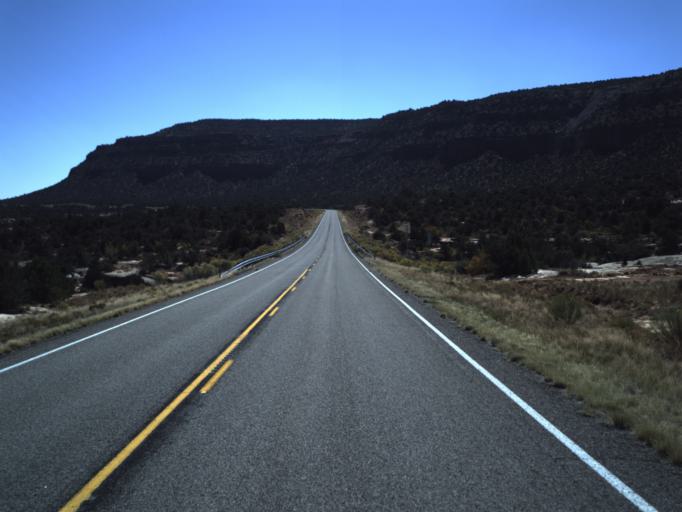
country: US
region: Utah
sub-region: San Juan County
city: Blanding
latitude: 37.6435
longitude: -110.1119
